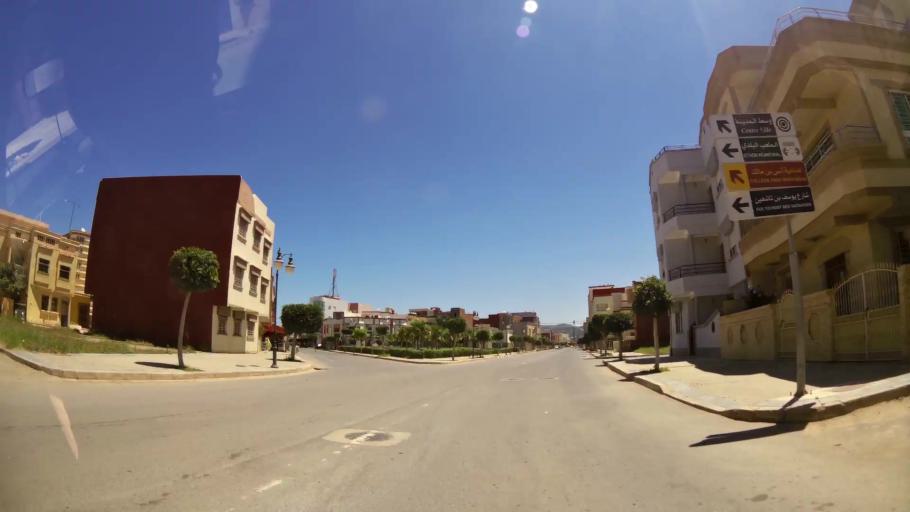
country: MA
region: Oriental
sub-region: Berkane-Taourirt
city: Madagh
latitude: 35.0807
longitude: -2.2356
